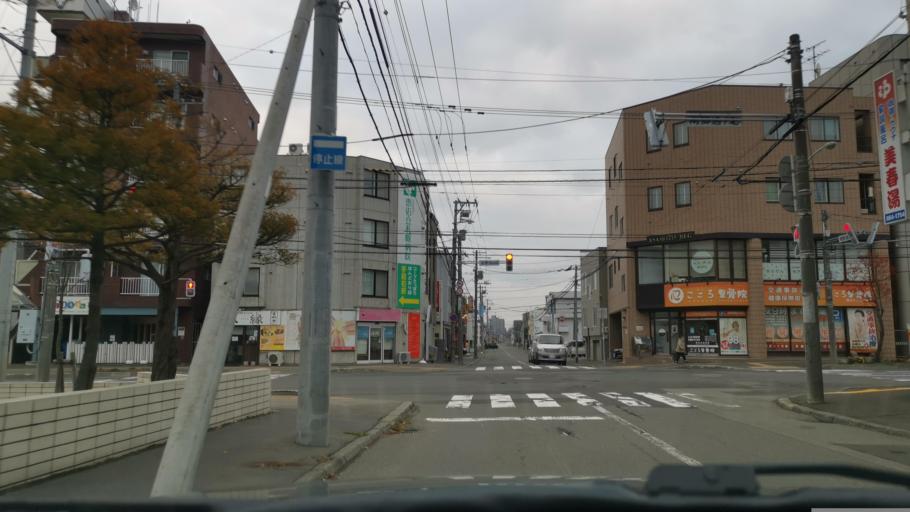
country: JP
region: Hokkaido
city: Sapporo
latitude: 43.0414
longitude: 141.4125
